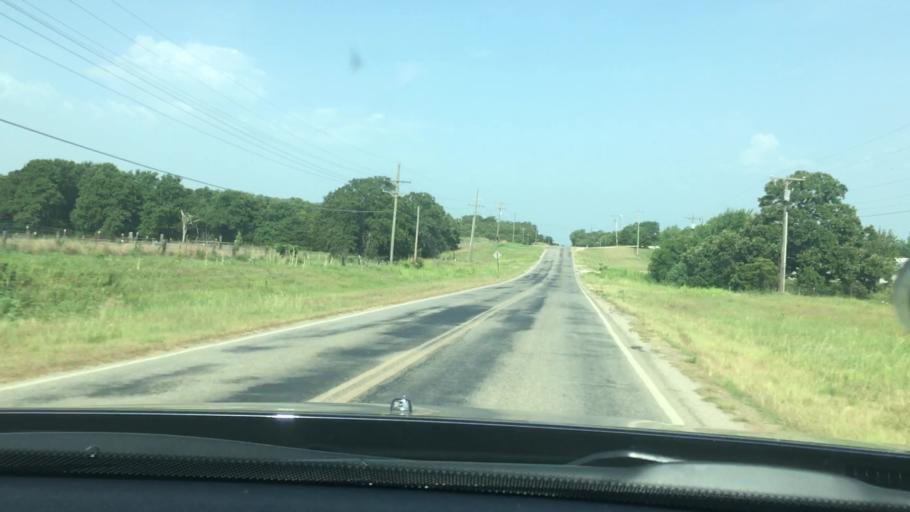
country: US
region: Oklahoma
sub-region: Pontotoc County
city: Byng
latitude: 34.8649
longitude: -96.6029
